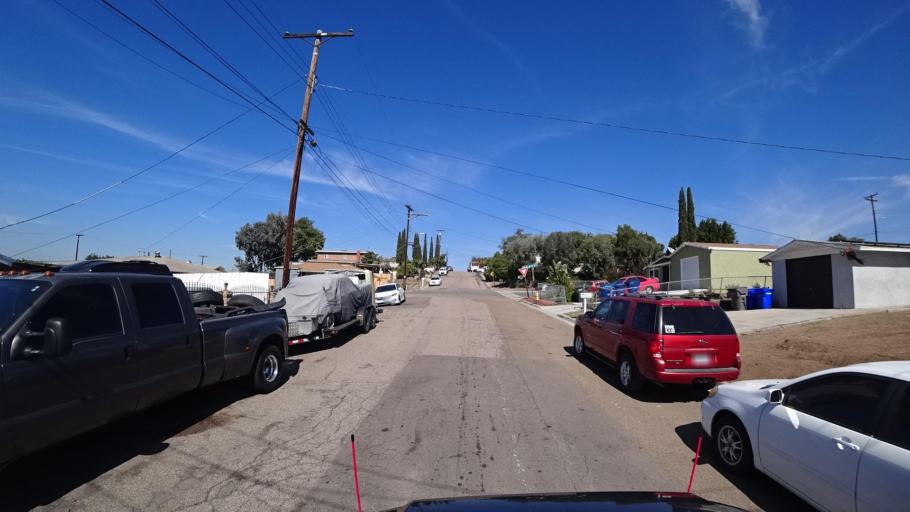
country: US
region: California
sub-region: San Diego County
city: La Presa
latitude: 32.7057
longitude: -117.0010
